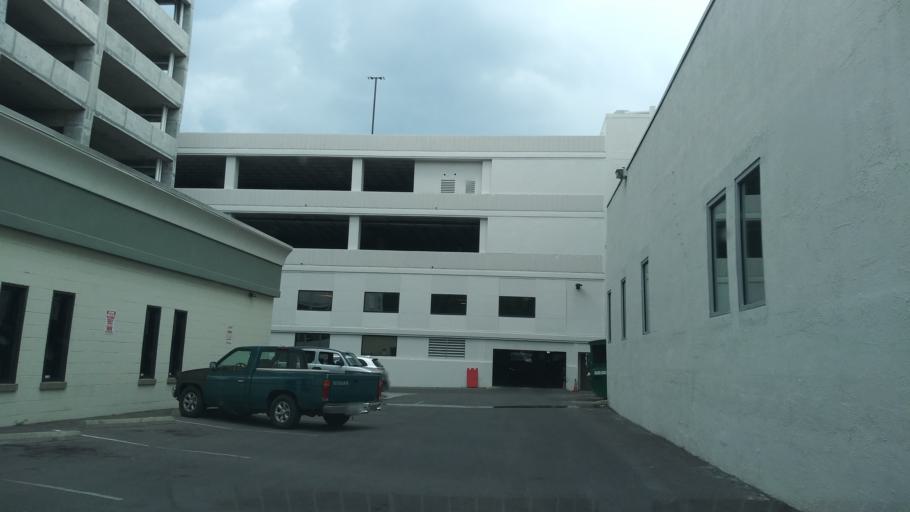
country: US
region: Tennessee
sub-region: Davidson County
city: Nashville
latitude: 36.1485
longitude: -86.8091
